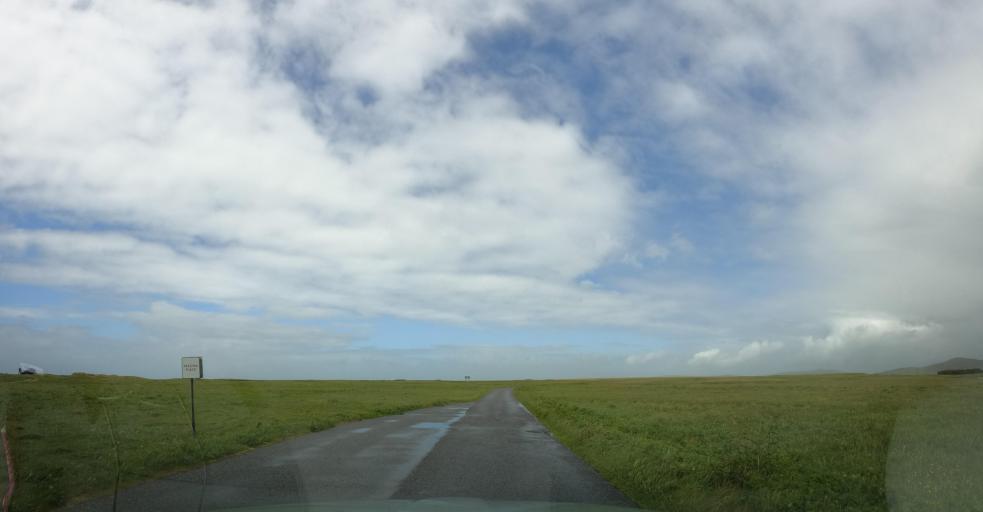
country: GB
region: Scotland
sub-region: Eilean Siar
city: Isle of South Uist
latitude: 57.2838
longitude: -7.4195
